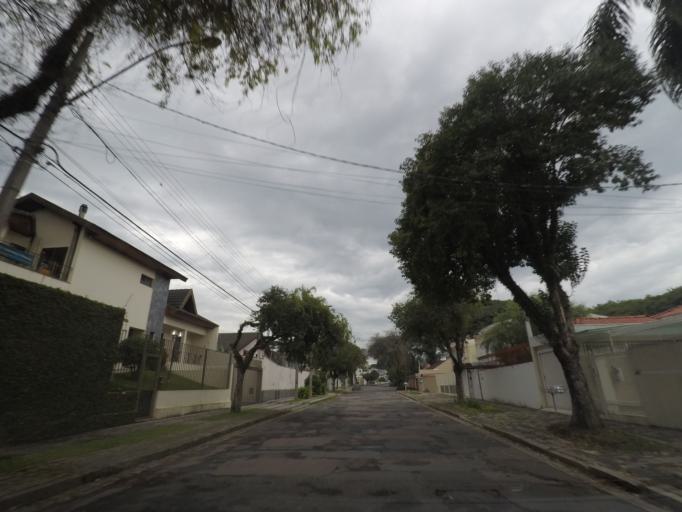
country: BR
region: Parana
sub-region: Curitiba
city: Curitiba
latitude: -25.4507
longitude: -49.3098
